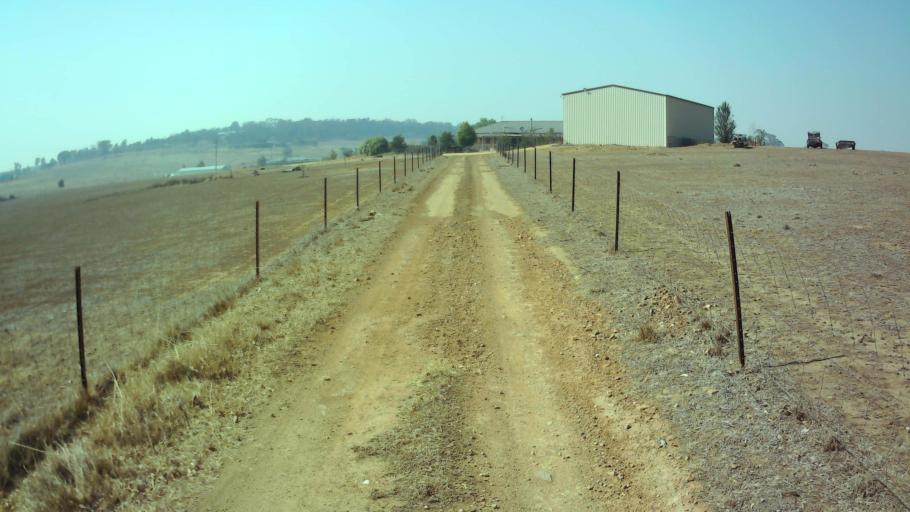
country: AU
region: New South Wales
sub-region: Weddin
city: Grenfell
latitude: -33.8965
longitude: 148.1794
